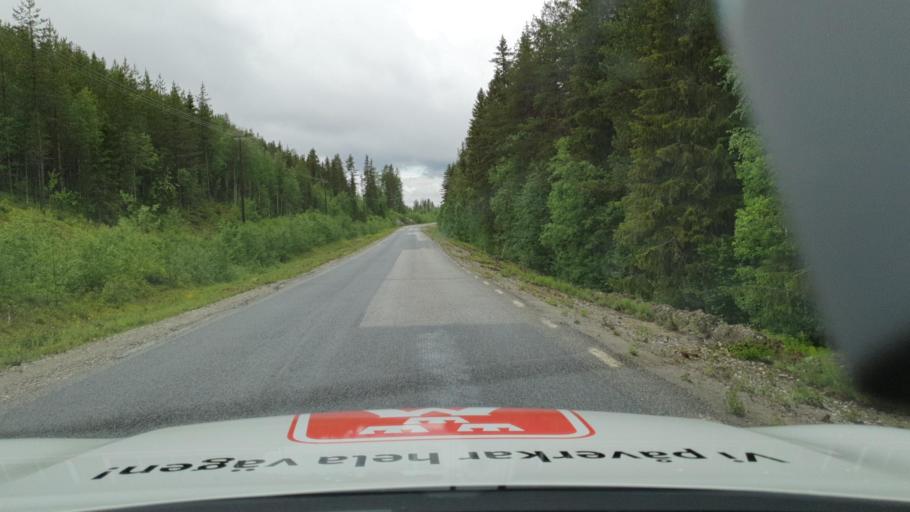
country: SE
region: Vaesterbotten
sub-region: Dorotea Kommun
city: Dorotea
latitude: 64.1753
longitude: 16.6434
